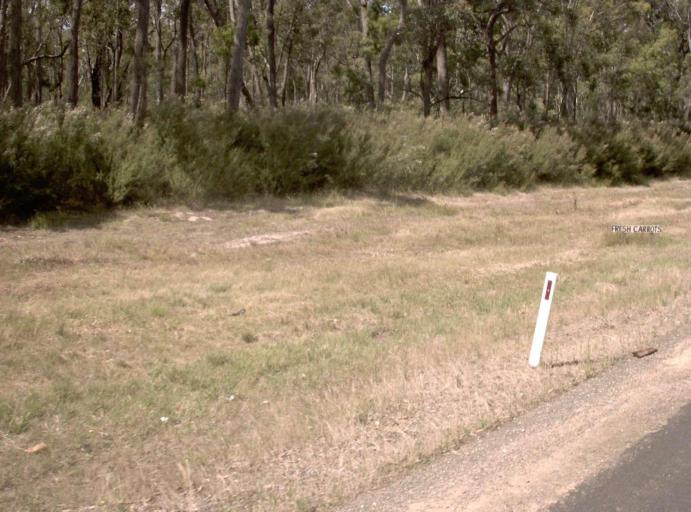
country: AU
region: Victoria
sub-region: Wellington
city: Sale
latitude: -37.9218
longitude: 147.2476
